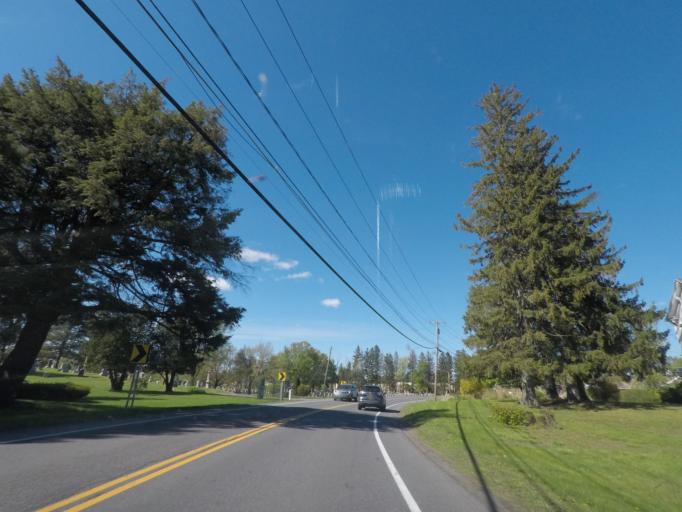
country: US
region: New York
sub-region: Albany County
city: Delmar
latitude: 42.5976
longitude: -73.7951
